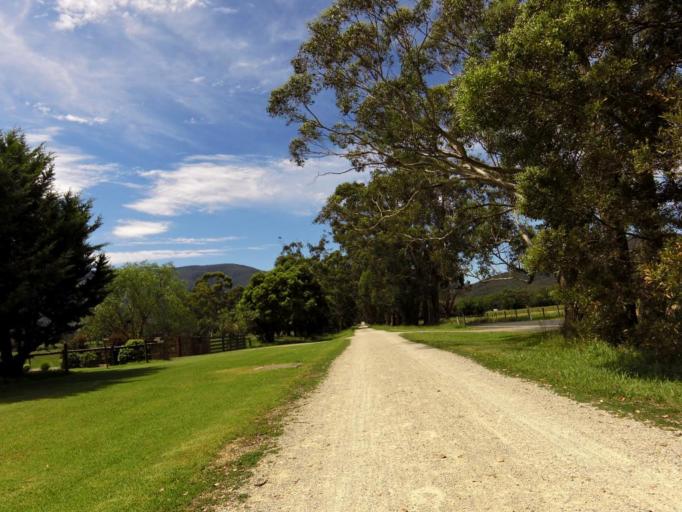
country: AU
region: Victoria
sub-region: Yarra Ranges
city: Yarra Junction
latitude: -37.7715
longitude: 145.6296
